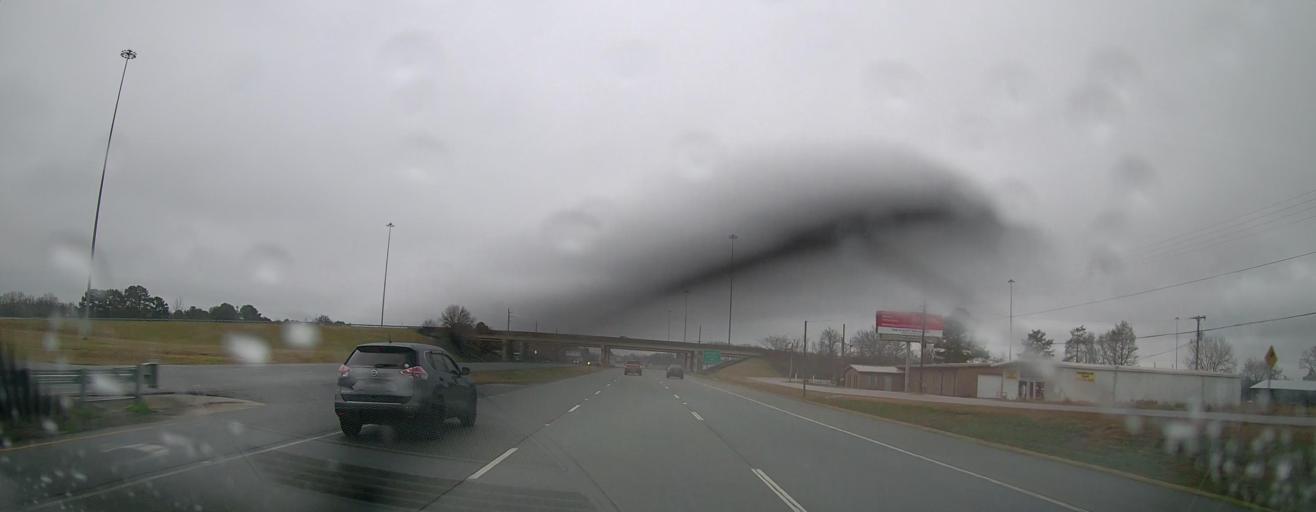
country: US
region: Alabama
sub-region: Morgan County
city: Decatur
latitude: 34.6036
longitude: -87.0314
